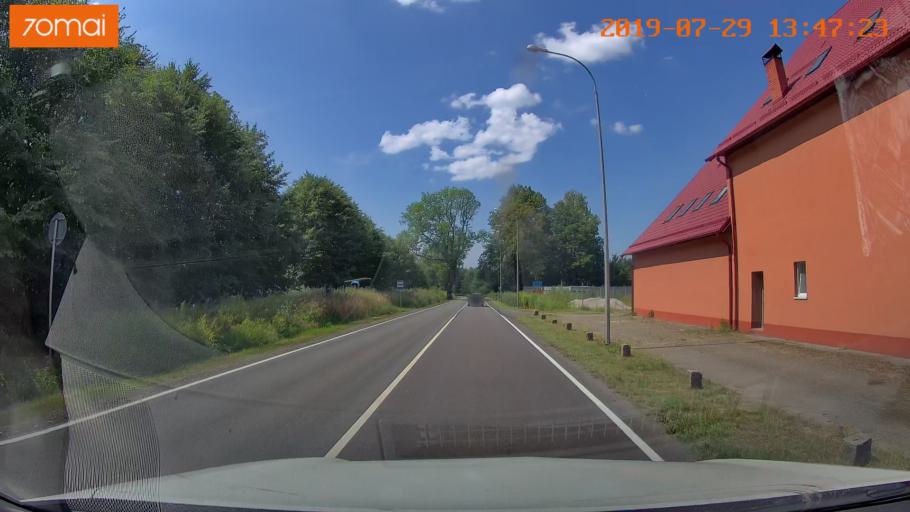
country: RU
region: Kaliningrad
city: Primorsk
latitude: 54.7398
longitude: 20.0488
